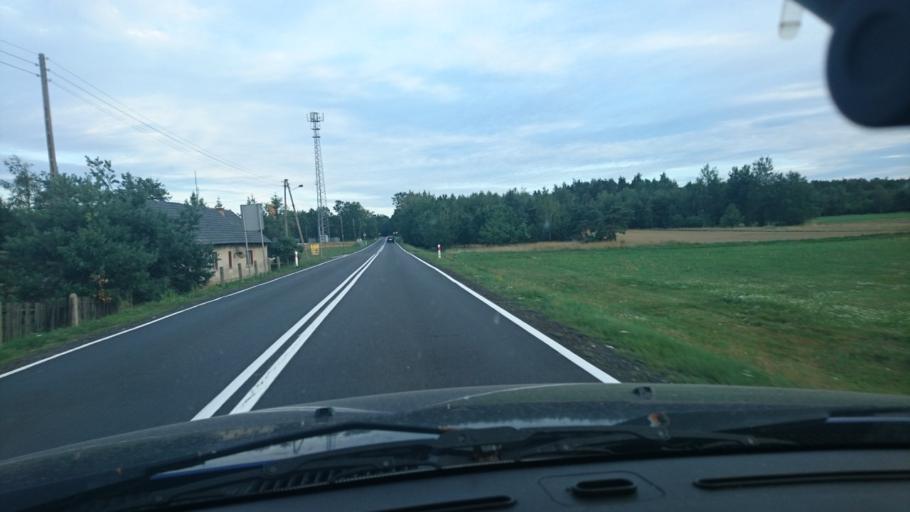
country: PL
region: Silesian Voivodeship
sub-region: Powiat lubliniecki
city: Sierakow Slaski
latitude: 50.8243
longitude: 18.5305
